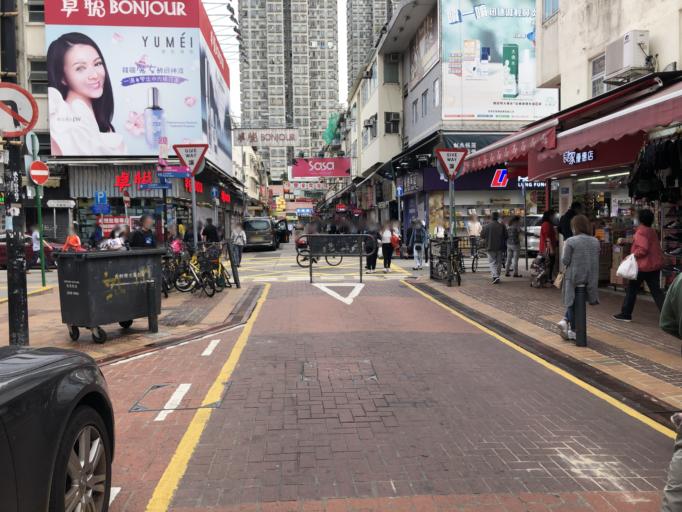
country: HK
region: Tai Po
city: Tai Po
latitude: 22.5043
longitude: 114.1287
